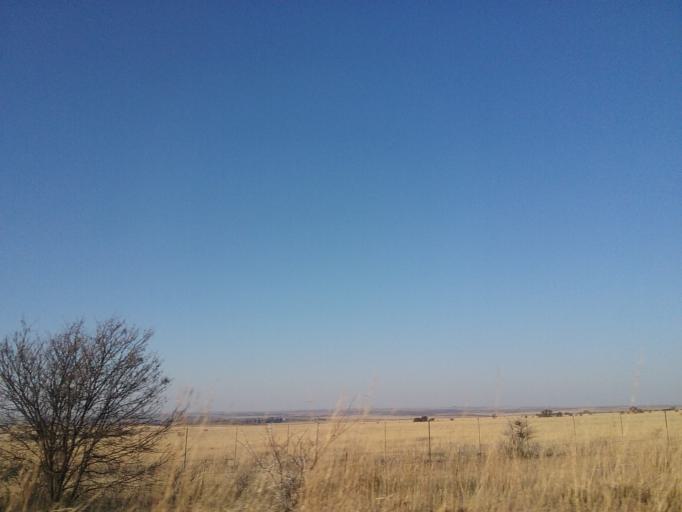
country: ZA
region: Orange Free State
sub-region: Fezile Dabi District Municipality
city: Kroonstad
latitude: -27.7841
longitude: 27.3187
